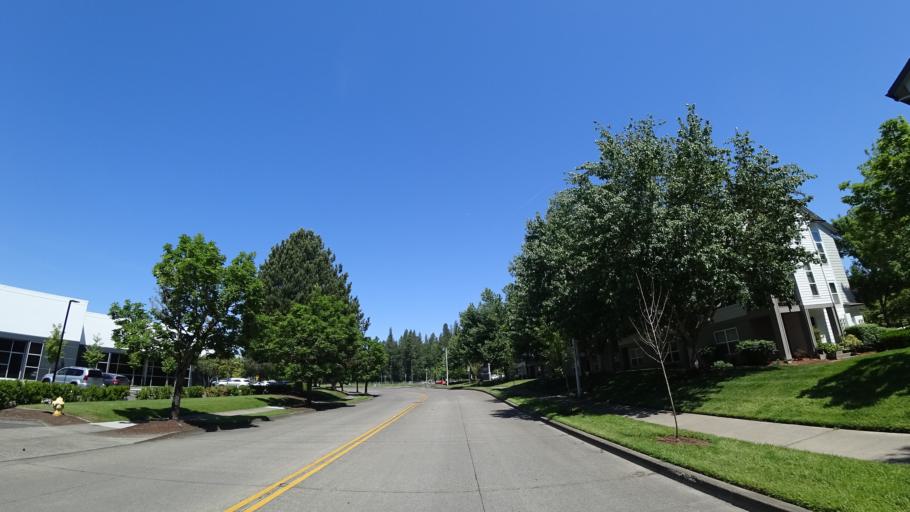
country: US
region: Oregon
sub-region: Washington County
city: Beaverton
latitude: 45.4983
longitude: -122.8335
